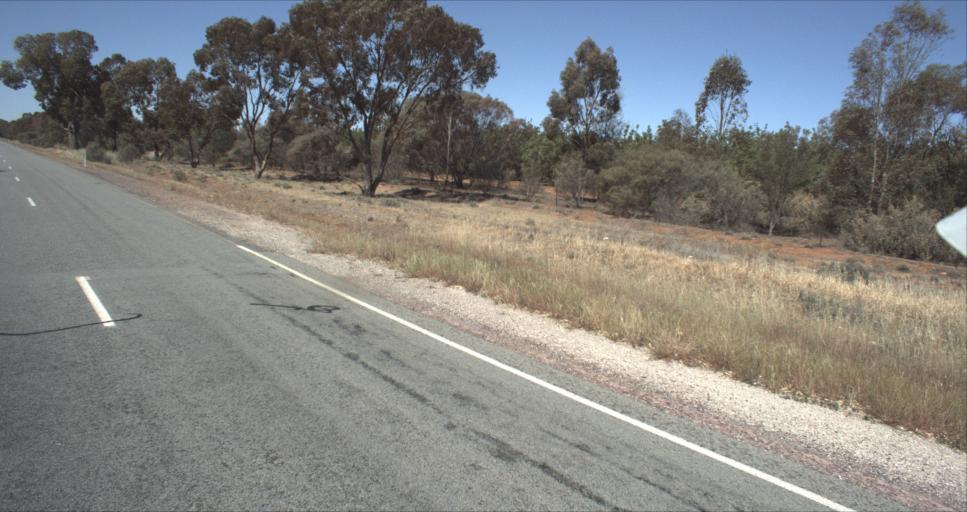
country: AU
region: New South Wales
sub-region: Leeton
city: Leeton
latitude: -34.4939
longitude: 146.4598
